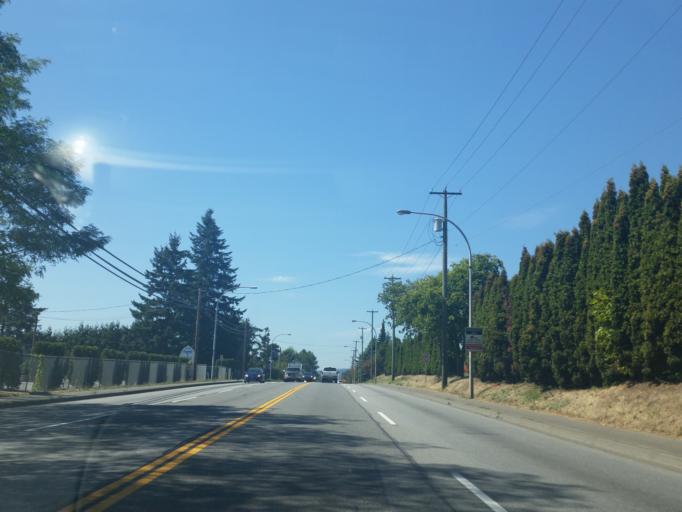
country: CA
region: British Columbia
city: Langley
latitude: 49.1042
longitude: -122.7056
